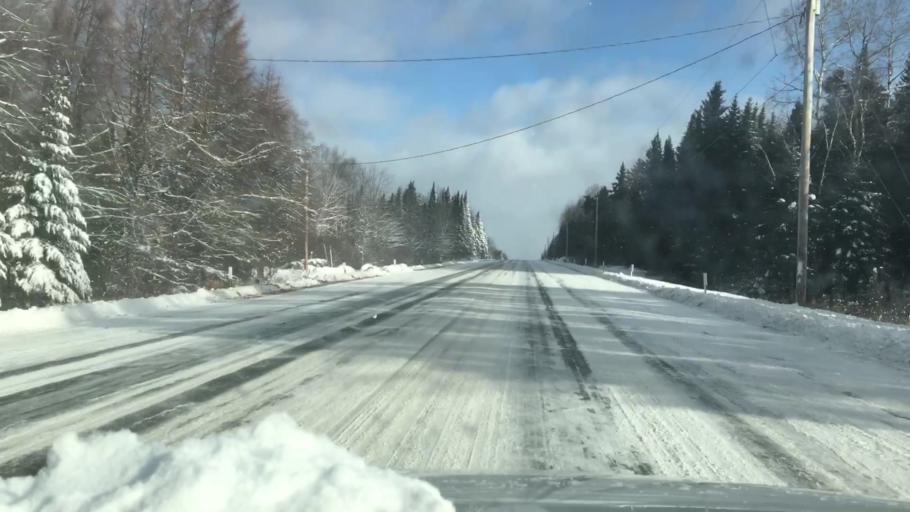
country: US
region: Maine
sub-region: Aroostook County
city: Van Buren
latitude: 47.0482
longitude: -67.9984
